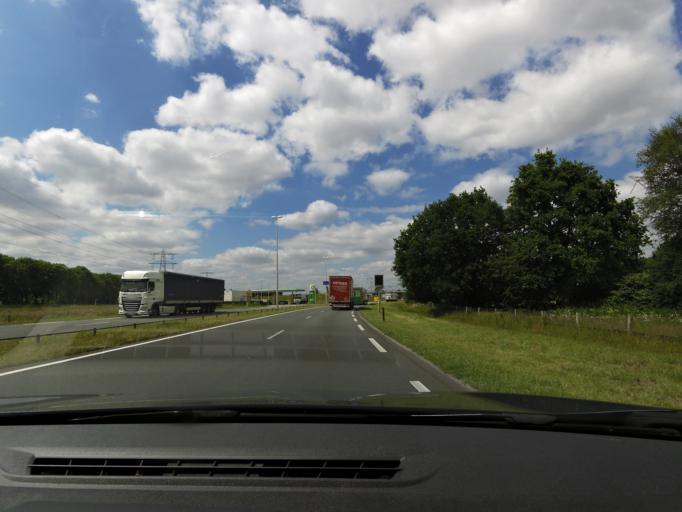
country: NL
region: North Brabant
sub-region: Gemeente Tilburg
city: Tilburg
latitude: 51.5838
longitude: 5.1114
